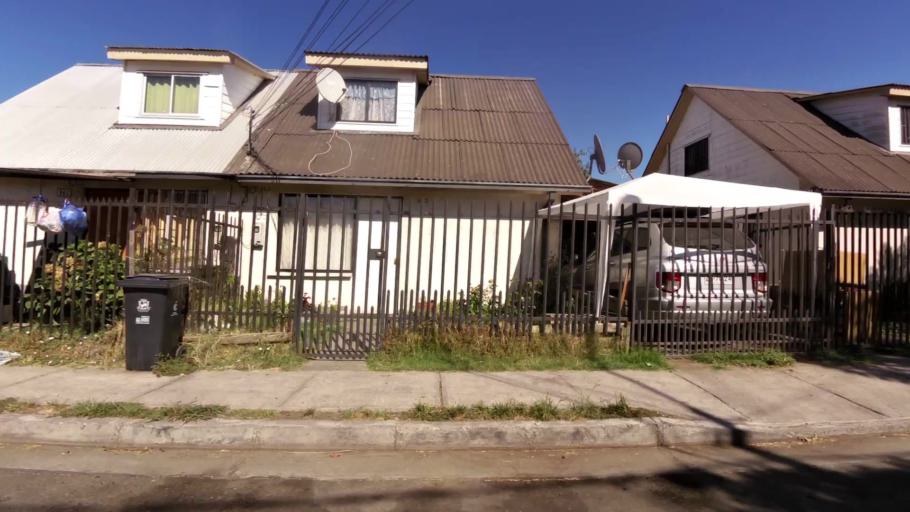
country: CL
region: Maule
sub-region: Provincia de Curico
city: Curico
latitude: -34.9799
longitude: -71.2674
